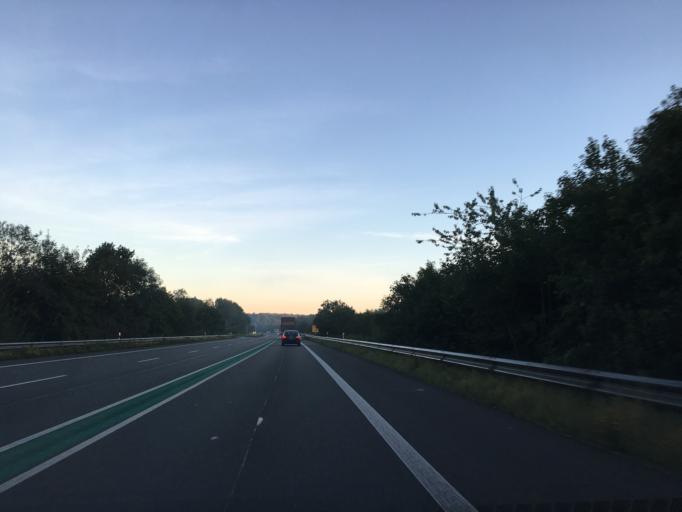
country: DE
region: North Rhine-Westphalia
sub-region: Regierungsbezirk Munster
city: Steinfurt
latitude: 52.1351
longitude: 7.3667
